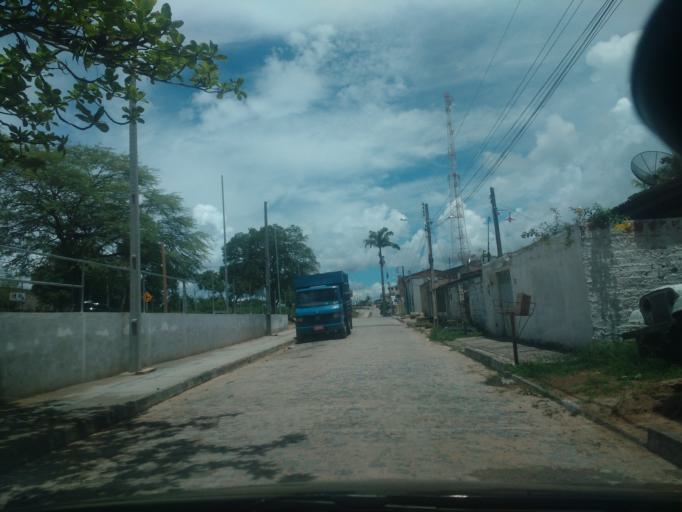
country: BR
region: Alagoas
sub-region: Uniao Dos Palmares
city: Uniao dos Palmares
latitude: -9.1645
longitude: -36.0198
